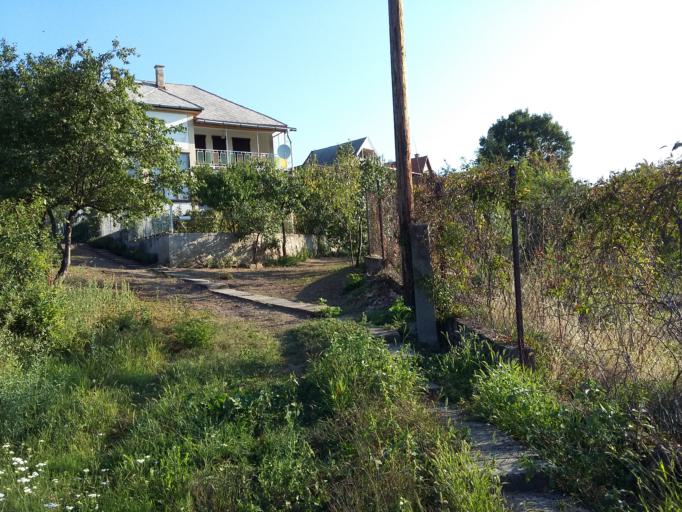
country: HU
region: Borsod-Abauj-Zemplen
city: Bekecs
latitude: 48.1520
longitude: 21.1696
